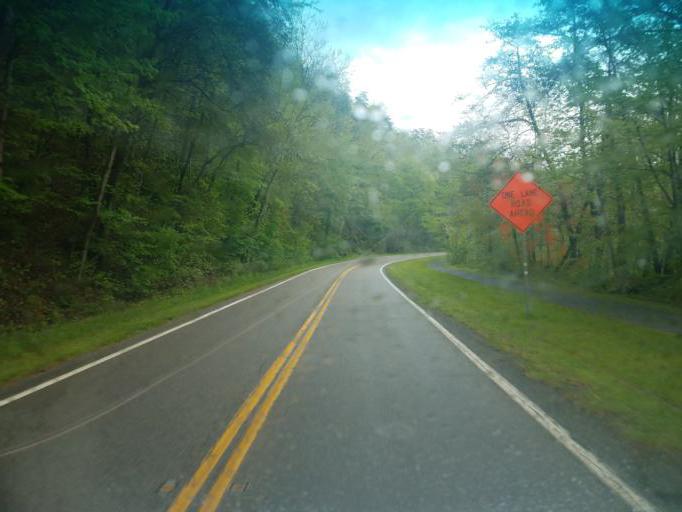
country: US
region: Virginia
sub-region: Washington County
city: Emory
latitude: 36.6297
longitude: -81.7790
